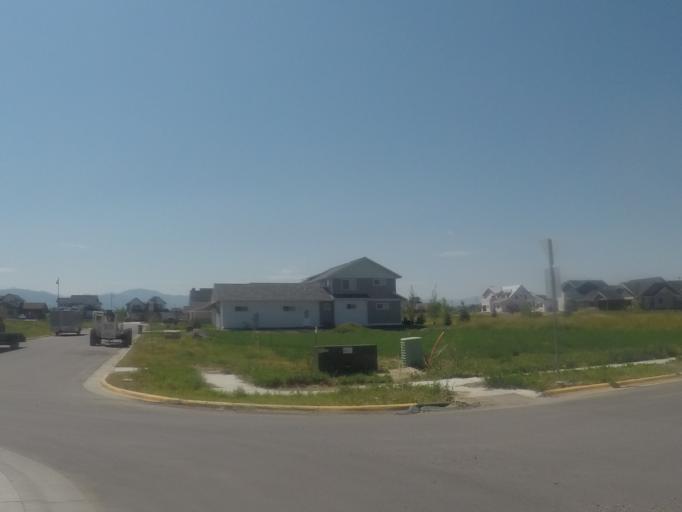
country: US
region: Montana
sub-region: Gallatin County
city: Bozeman
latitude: 45.6897
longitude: -111.0961
